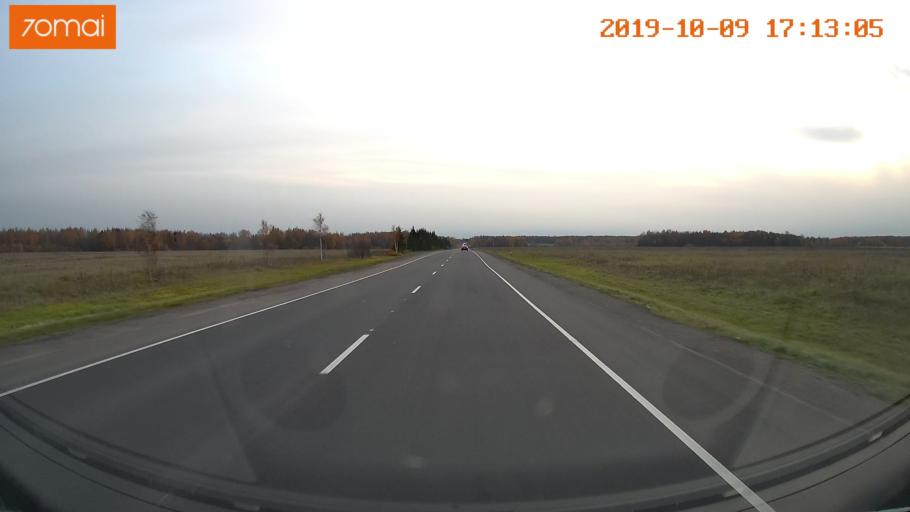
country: RU
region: Ivanovo
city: Privolzhsk
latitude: 57.3196
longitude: 41.2301
